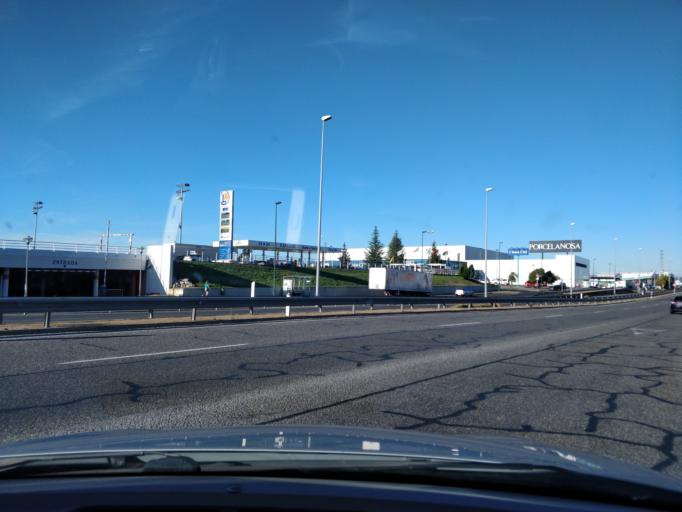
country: ES
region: Castille and Leon
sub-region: Provincia de Leon
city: San Andres del Rabanedo
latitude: 42.5893
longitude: -5.6190
